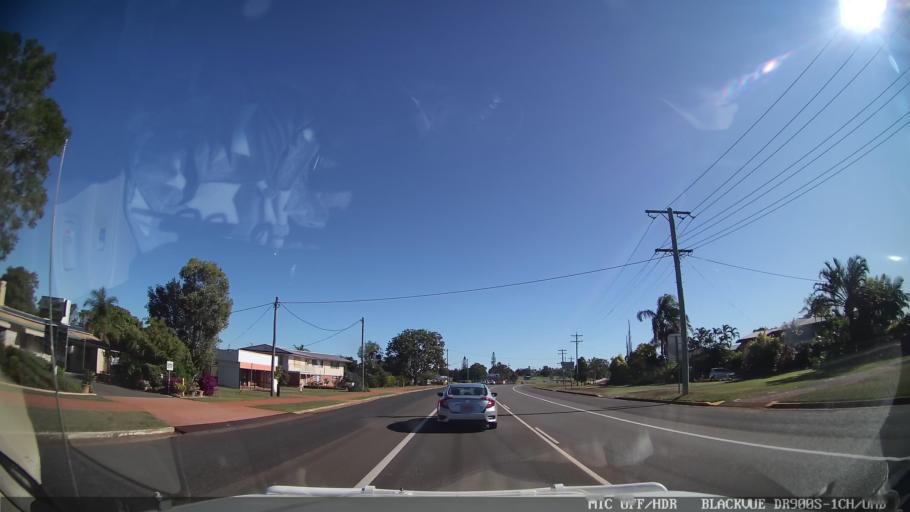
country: AU
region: Queensland
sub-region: Bundaberg
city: Childers
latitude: -25.2336
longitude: 152.2690
